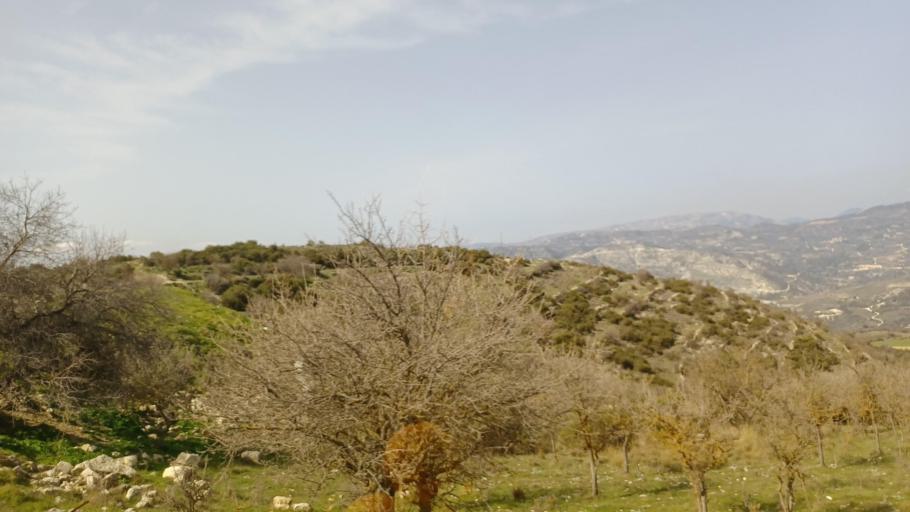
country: CY
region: Limassol
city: Pachna
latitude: 34.8000
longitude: 32.7423
